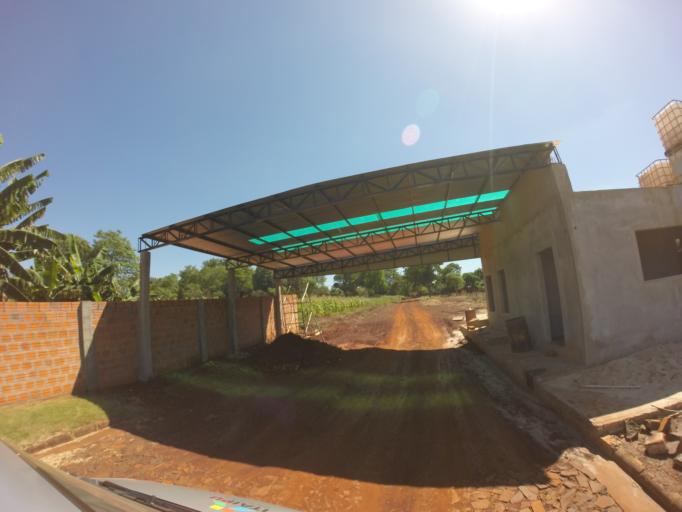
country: PY
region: Alto Parana
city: Ciudad del Este
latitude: -25.4376
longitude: -54.6466
